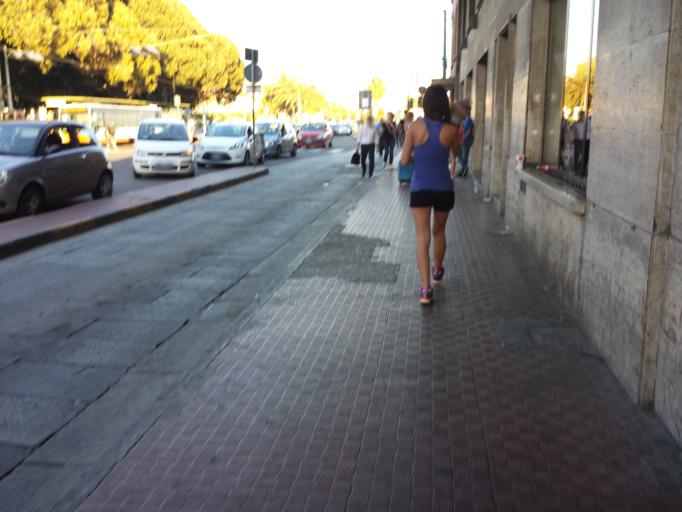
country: IT
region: Sardinia
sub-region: Provincia di Cagliari
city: Cagliari
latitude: 39.2151
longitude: 9.1090
